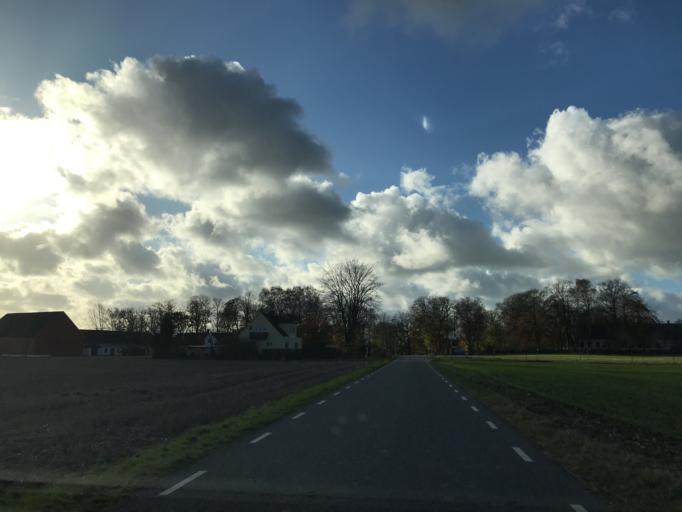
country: SE
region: Skane
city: Smygehamn
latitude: 55.3840
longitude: 13.4255
